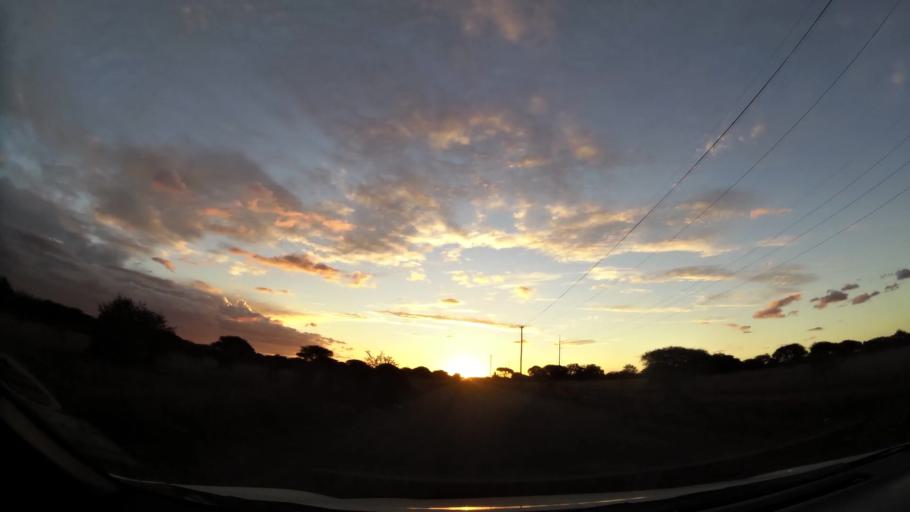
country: ZA
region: Limpopo
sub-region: Capricorn District Municipality
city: Polokwane
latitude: -23.7440
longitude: 29.4603
